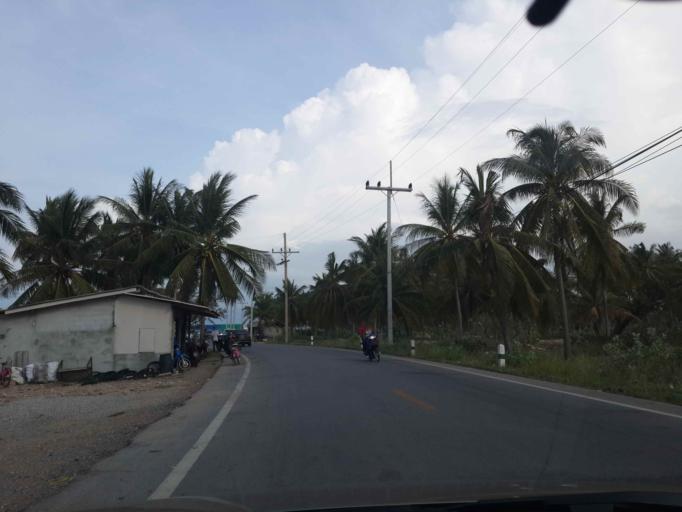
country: TH
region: Pattani
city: Yaring
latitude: 6.9187
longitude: 101.3337
